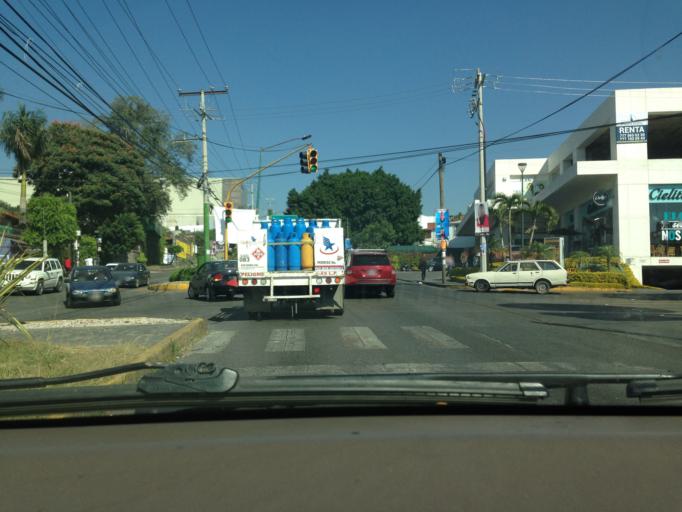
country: MX
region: Morelos
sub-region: Cuernavaca
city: Fraccionamiento Lomas de Ahuatlan
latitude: 18.9527
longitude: -99.2359
